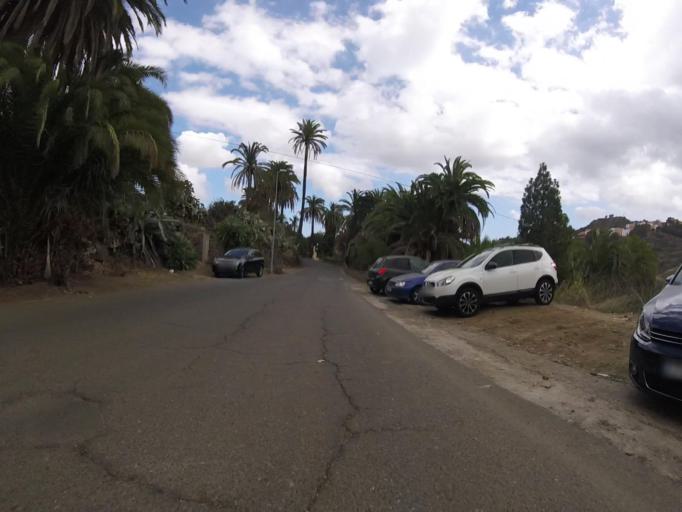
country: ES
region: Canary Islands
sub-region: Provincia de Las Palmas
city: Santa Brigida
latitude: 28.0409
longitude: -15.4904
